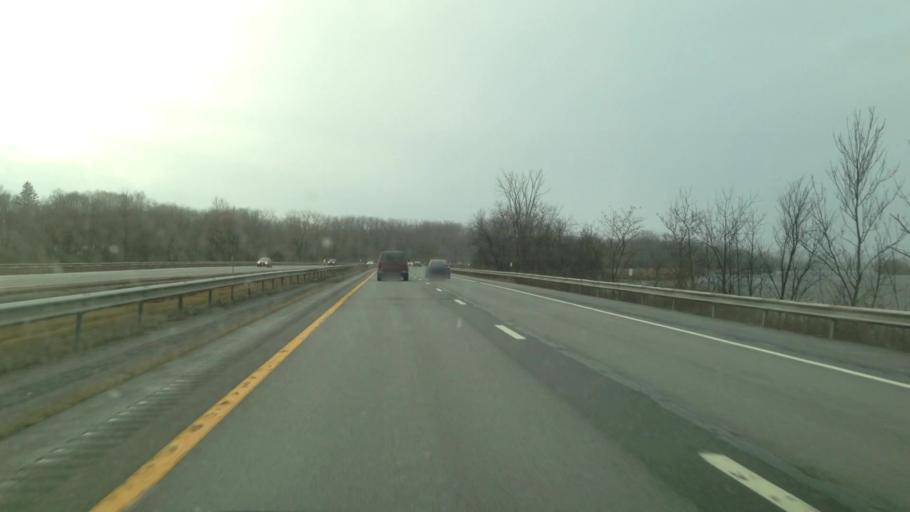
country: US
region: New York
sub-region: Montgomery County
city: Tribes Hill
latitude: 42.9304
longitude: -74.3019
